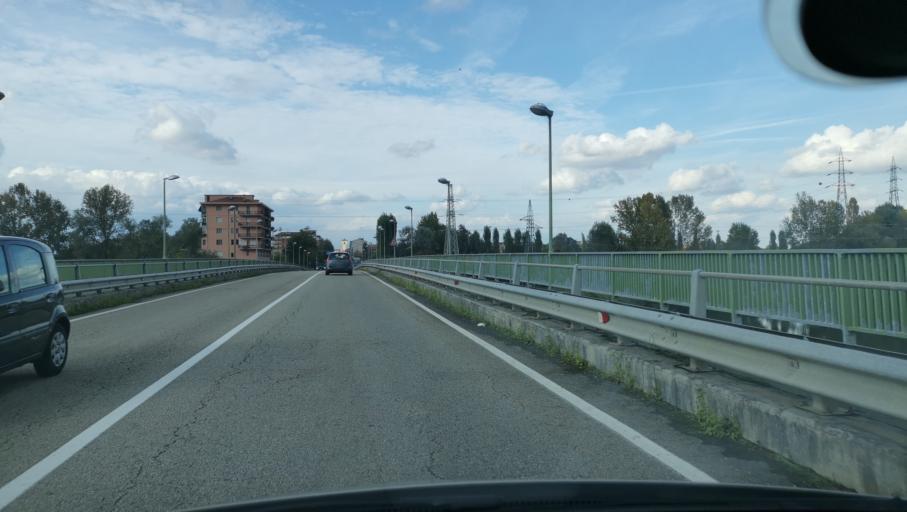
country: IT
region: Piedmont
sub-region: Provincia di Torino
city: Chivasso
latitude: 45.1806
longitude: 7.8904
